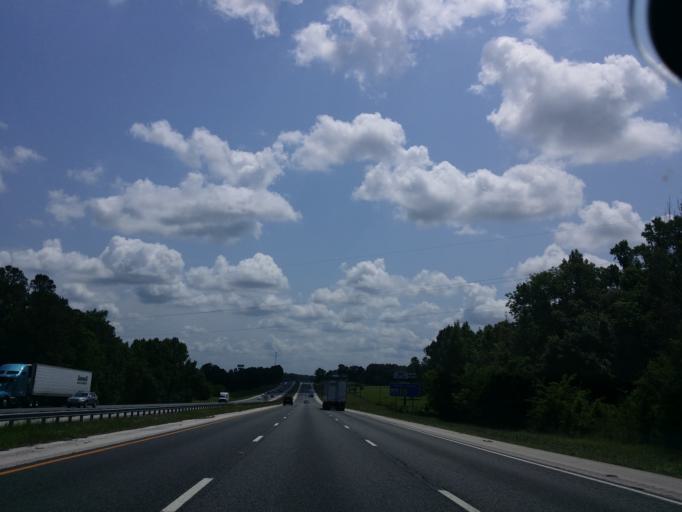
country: US
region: Florida
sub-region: Marion County
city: Citra
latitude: 29.4181
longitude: -82.2559
